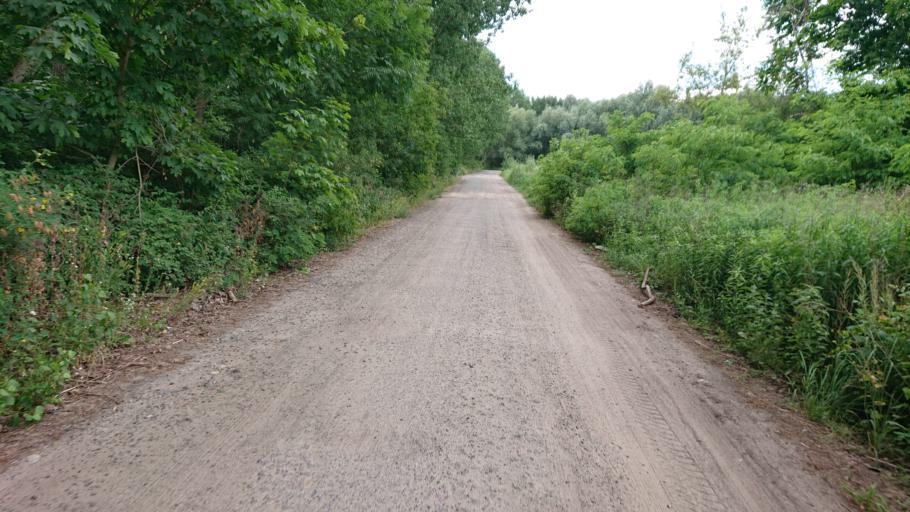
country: DE
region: Brandenburg
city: Potsdam
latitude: 52.3690
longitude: 13.1077
